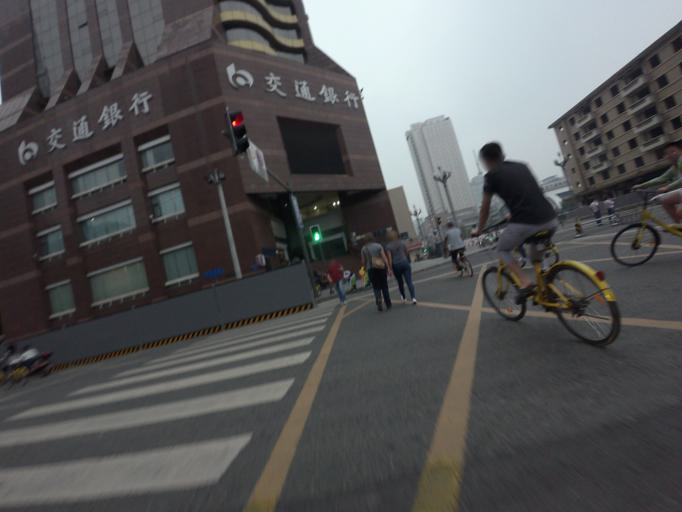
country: CN
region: Sichuan
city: Chengdu
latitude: 30.6695
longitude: 104.0633
